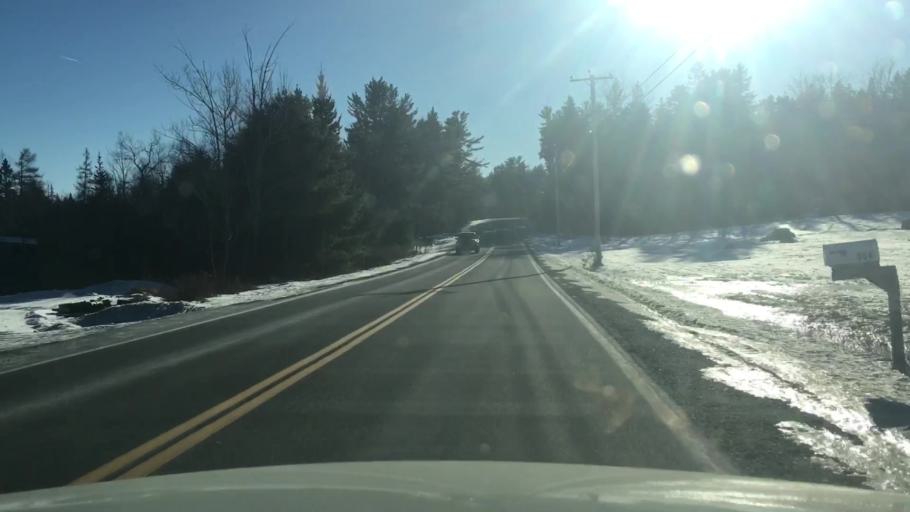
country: US
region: Maine
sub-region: Hancock County
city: Orland
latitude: 44.5189
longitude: -68.7499
